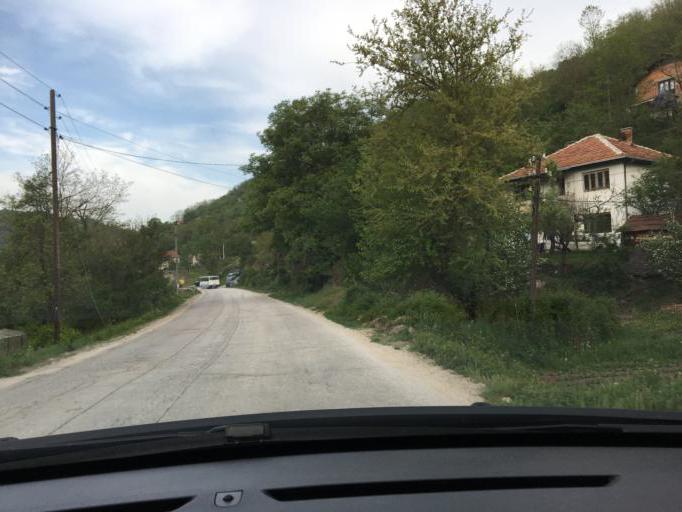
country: MK
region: Kriva Palanka
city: Kriva Palanka
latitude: 42.2253
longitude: 22.4040
